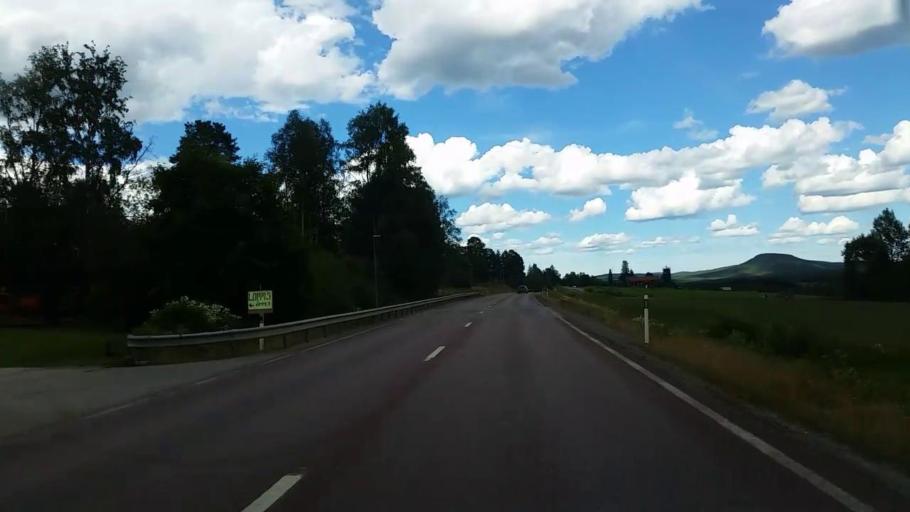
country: SE
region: Gaevleborg
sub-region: Ljusdals Kommun
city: Jaervsoe
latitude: 61.6931
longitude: 16.1544
